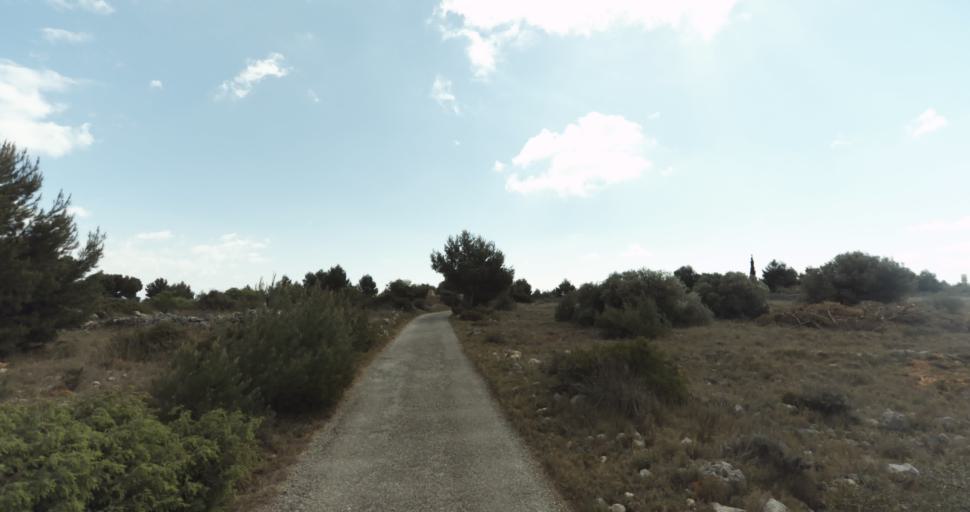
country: FR
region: Languedoc-Roussillon
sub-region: Departement de l'Aude
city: Leucate
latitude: 42.9185
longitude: 3.0516
